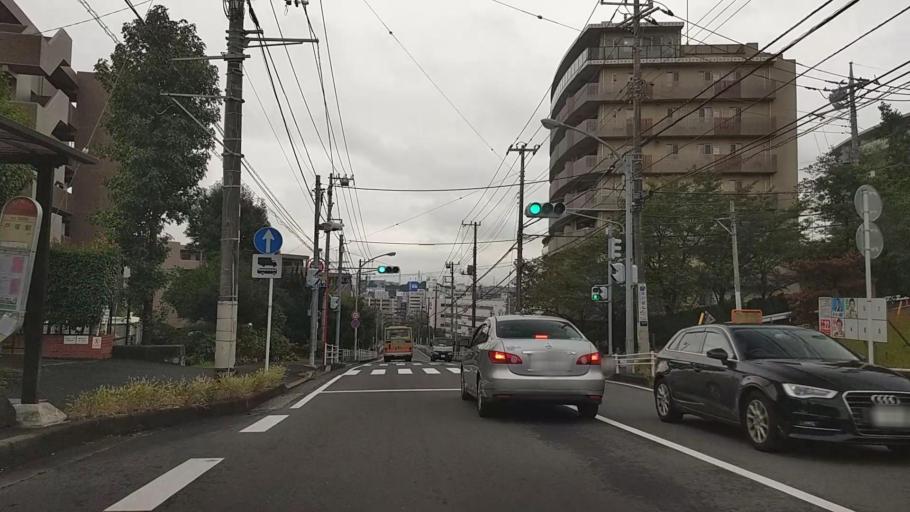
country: JP
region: Kanagawa
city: Kamakura
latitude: 35.3994
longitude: 139.5441
